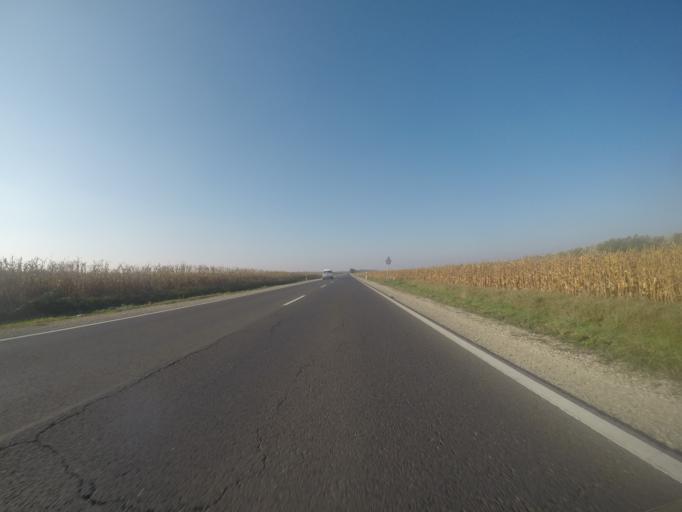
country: HU
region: Fejer
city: Ercsi
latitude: 47.2689
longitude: 18.8854
